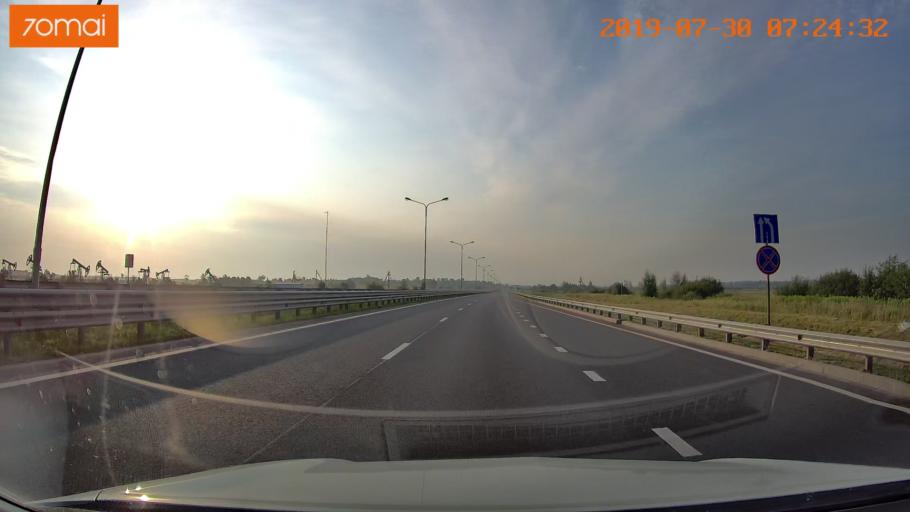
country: RU
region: Kaliningrad
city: Bol'shoe Isakovo
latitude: 54.6930
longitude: 20.8131
